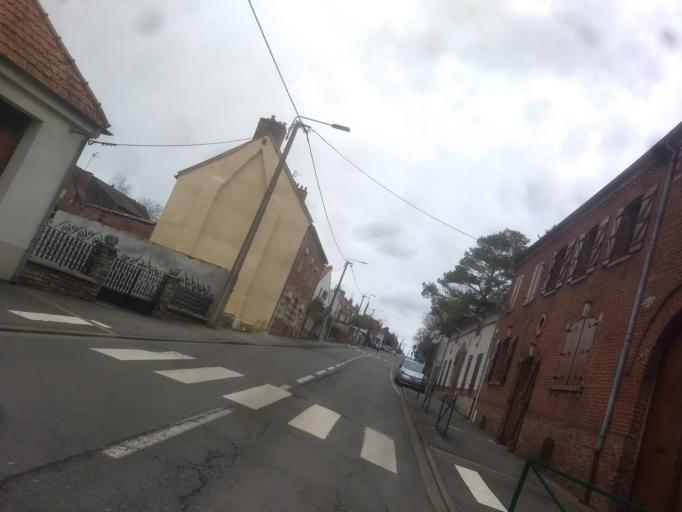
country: FR
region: Nord-Pas-de-Calais
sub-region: Departement du Pas-de-Calais
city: Sainte-Catherine
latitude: 50.3041
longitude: 2.7609
